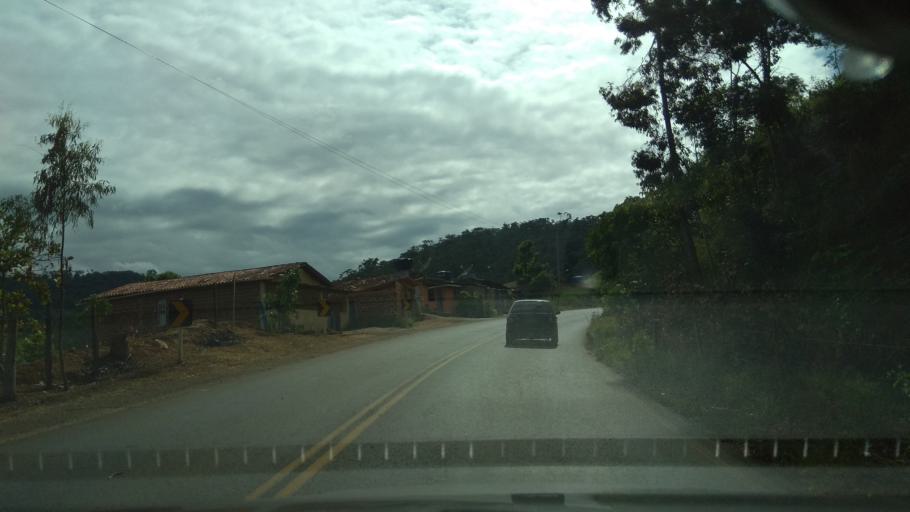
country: BR
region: Bahia
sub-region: Ubaira
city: Ubaira
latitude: -13.2691
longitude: -39.6298
